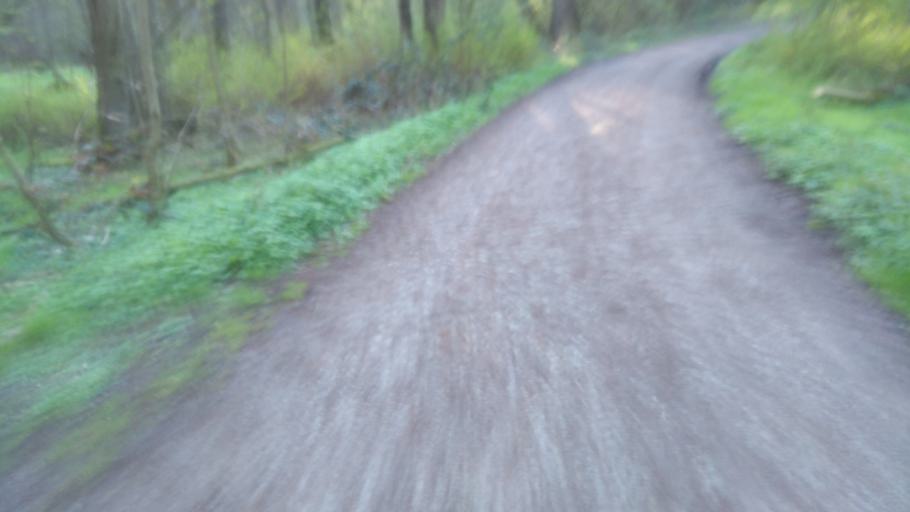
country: DE
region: Lower Saxony
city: Nottensdorf
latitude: 53.4772
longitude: 9.6271
